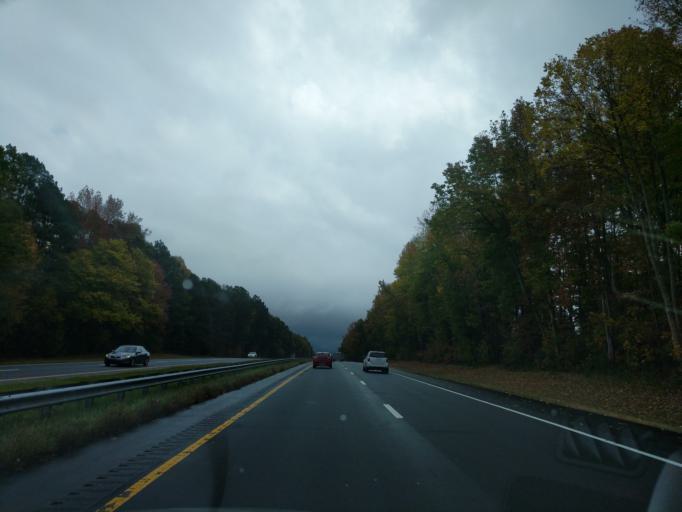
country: US
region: North Carolina
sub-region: Orange County
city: Hillsborough
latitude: 36.0527
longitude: -79.0641
